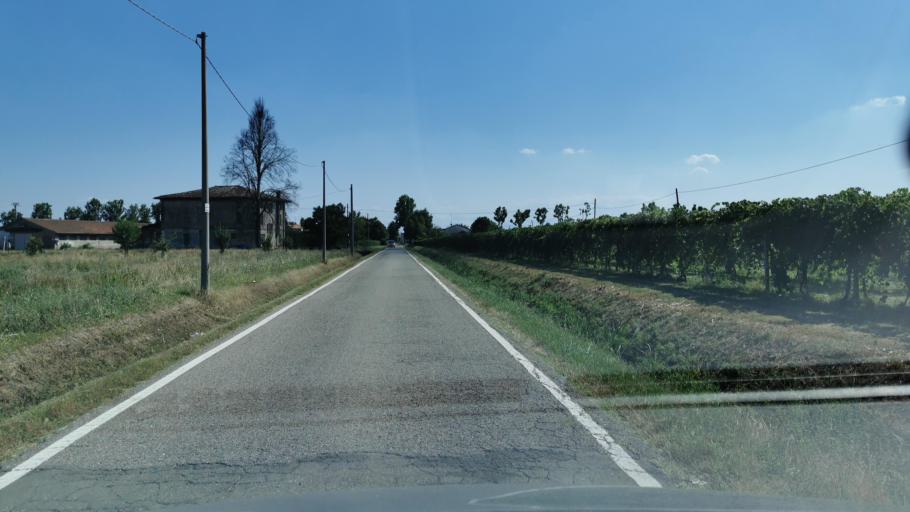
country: IT
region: Emilia-Romagna
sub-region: Provincia di Modena
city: Limidi
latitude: 44.7692
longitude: 10.9169
